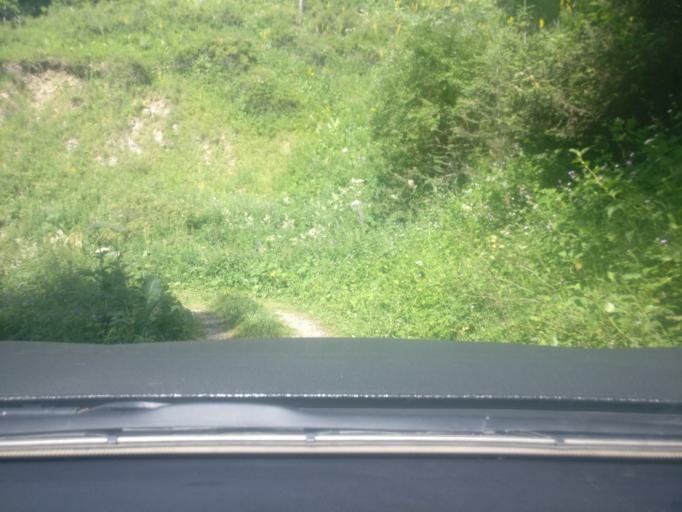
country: KZ
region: Almaty Qalasy
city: Almaty
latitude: 43.1055
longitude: 76.9525
